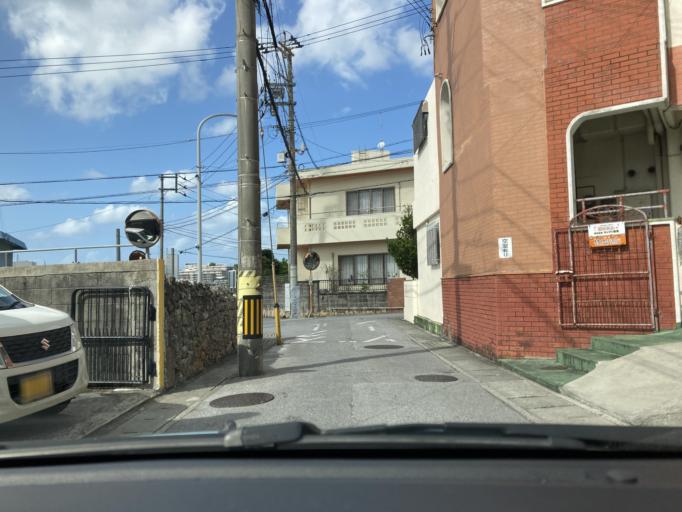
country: JP
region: Okinawa
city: Naha-shi
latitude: 26.2119
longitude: 127.7128
